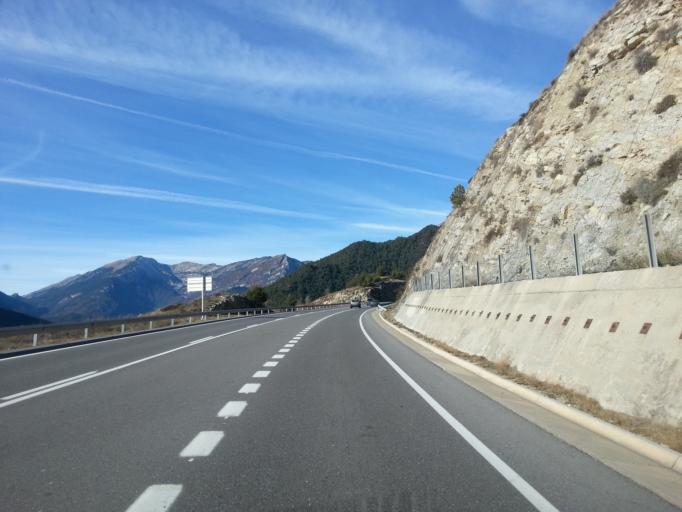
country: ES
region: Catalonia
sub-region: Provincia de Barcelona
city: Baga
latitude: 42.2588
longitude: 1.8576
